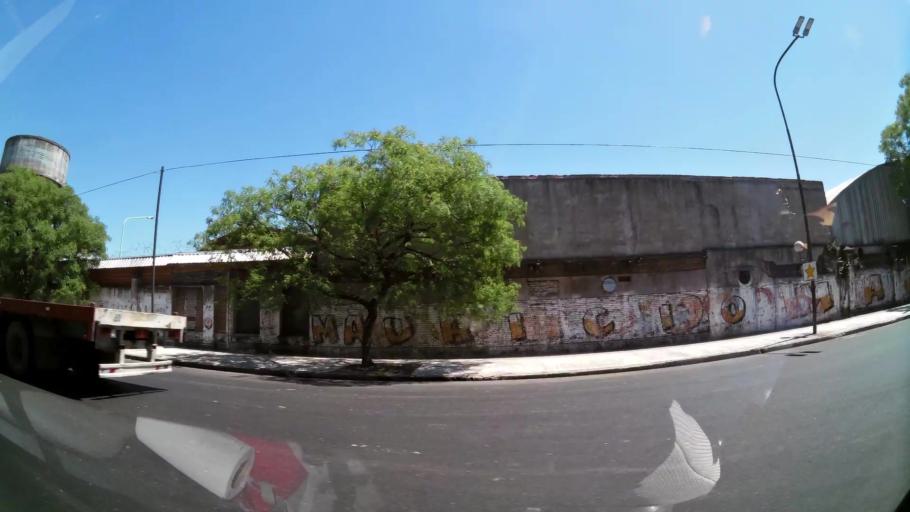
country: AR
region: Buenos Aires
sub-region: Partido de Avellaneda
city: Avellaneda
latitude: -34.6446
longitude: -58.4012
